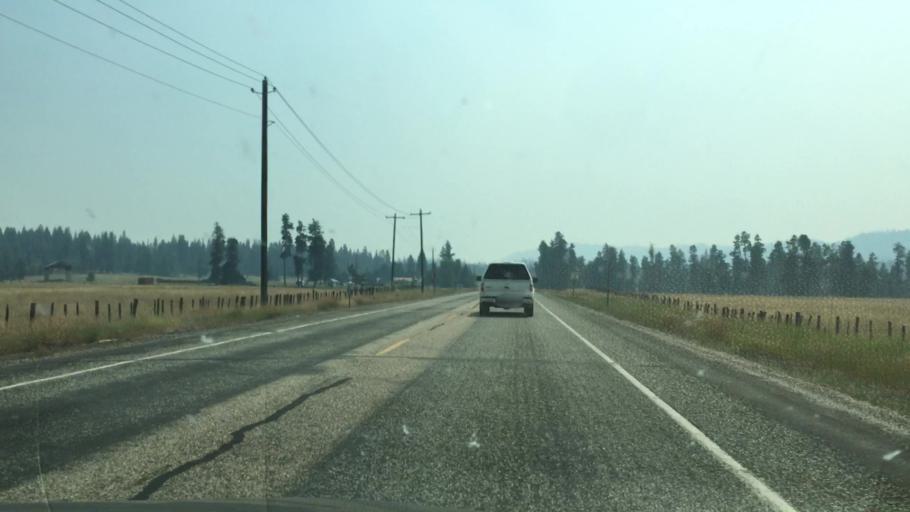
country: US
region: Idaho
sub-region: Valley County
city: Cascade
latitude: 44.3961
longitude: -116.0055
